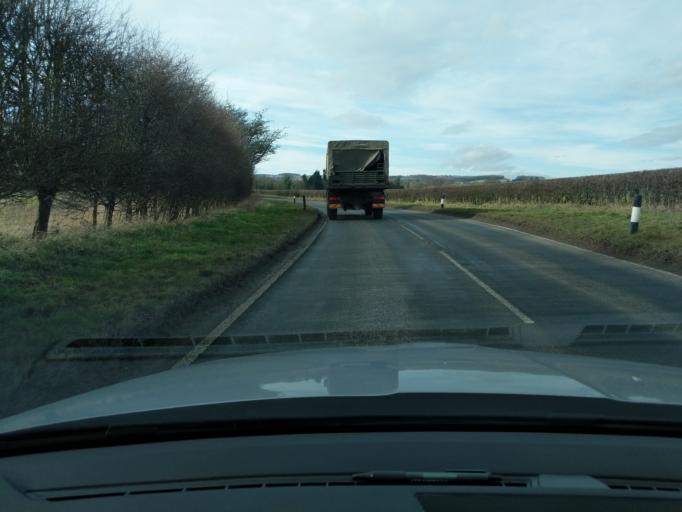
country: GB
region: England
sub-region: North Yorkshire
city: Catterick Garrison
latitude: 54.3947
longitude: -1.6819
